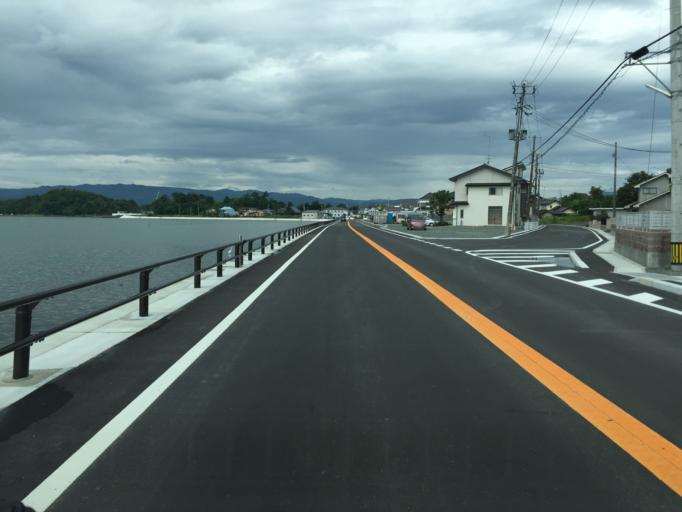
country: JP
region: Miyagi
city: Marumori
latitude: 37.8230
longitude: 140.9588
